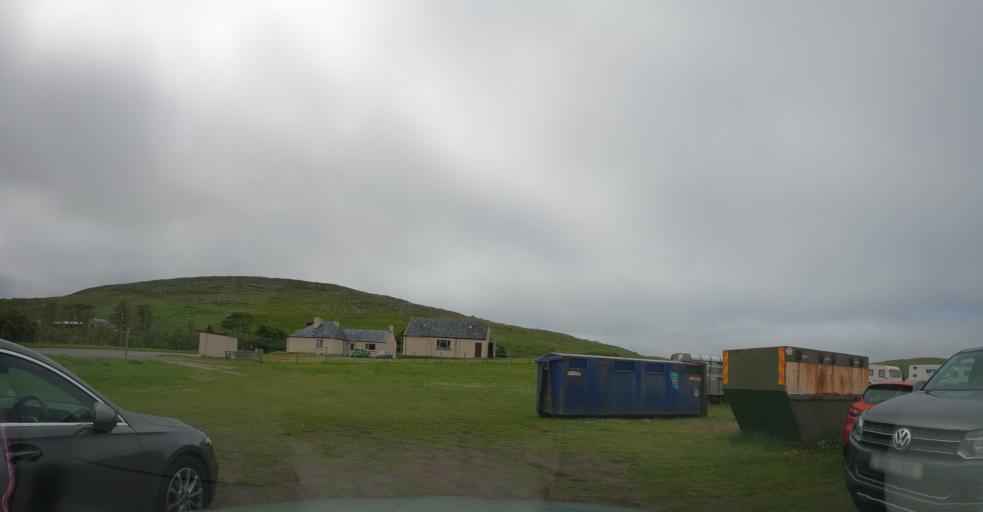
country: GB
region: Scotland
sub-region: Eilean Siar
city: Harris
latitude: 57.8618
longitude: -6.9777
